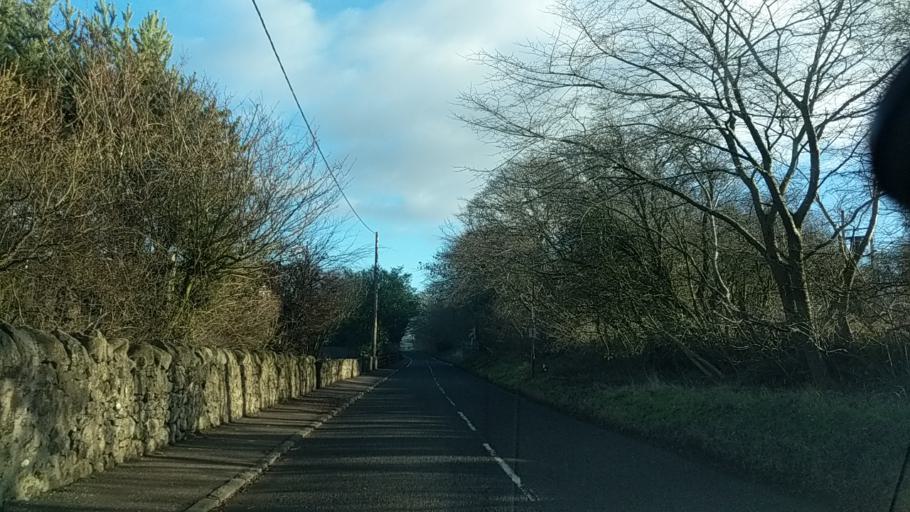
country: GB
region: Scotland
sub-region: West Lothian
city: Broxburn
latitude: 55.9778
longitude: -3.5207
